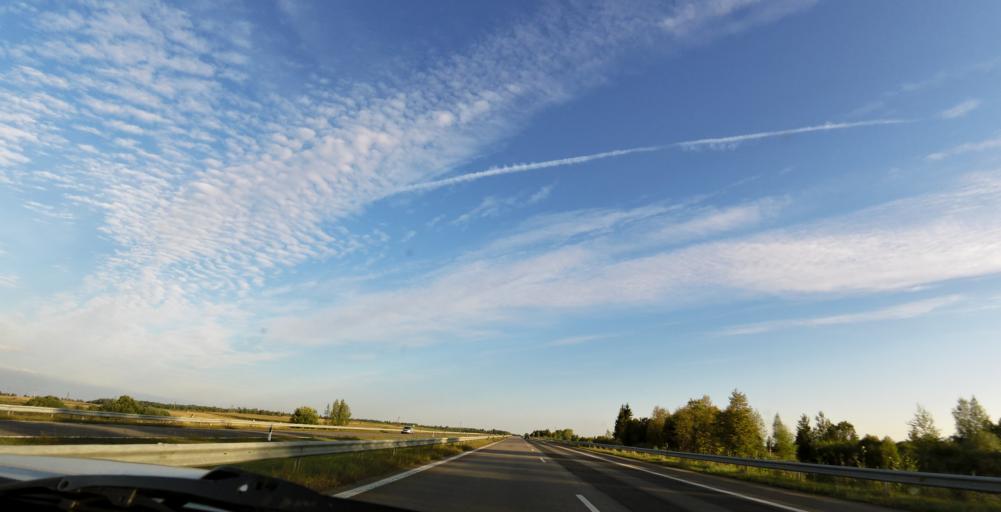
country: LT
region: Vilnius County
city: Ukmerge
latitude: 55.1567
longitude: 24.8211
